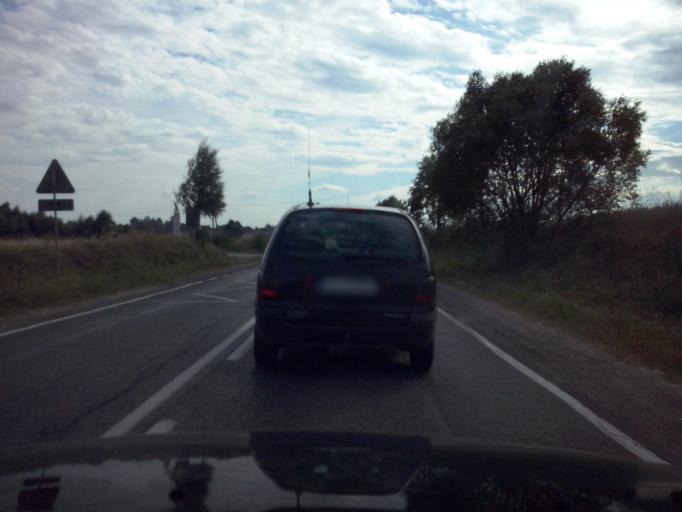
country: PL
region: Swietokrzyskie
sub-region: Powiat kielecki
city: Lagow
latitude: 50.7498
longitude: 21.0732
